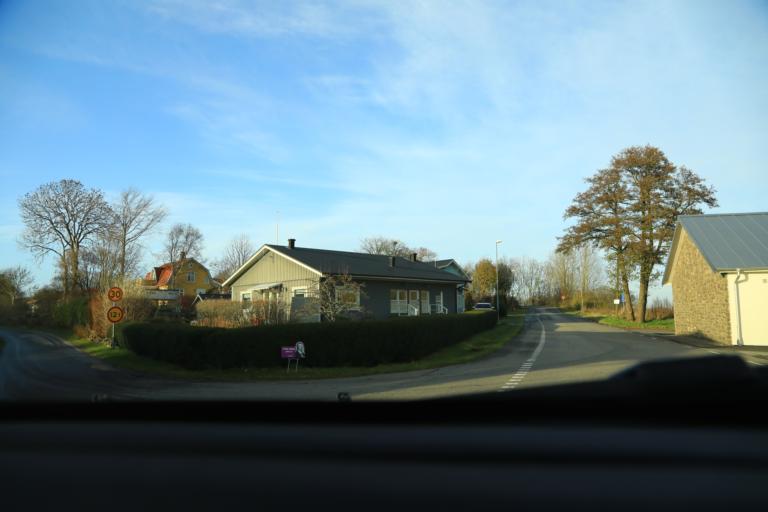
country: SE
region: Halland
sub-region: Varbergs Kommun
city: Varberg
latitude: 57.1912
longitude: 12.2203
